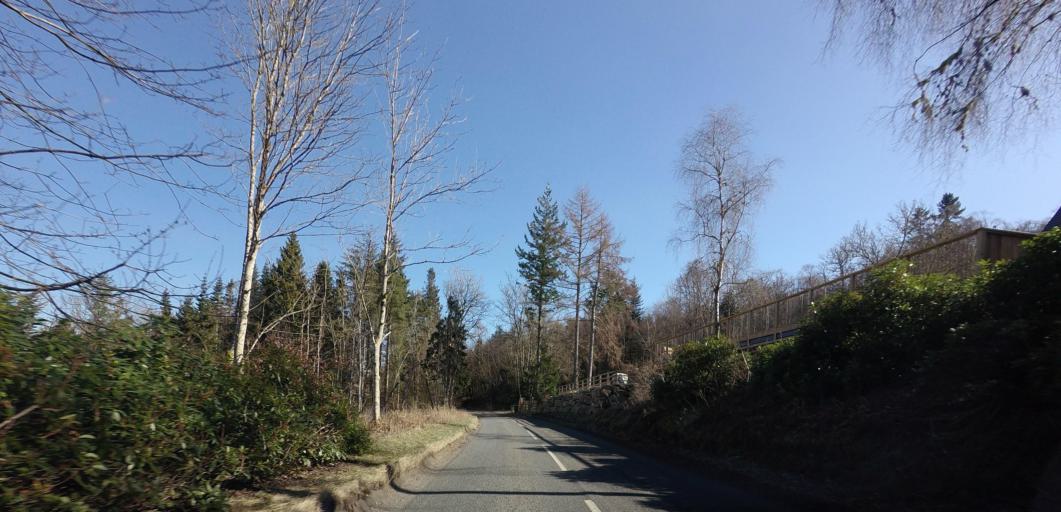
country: GB
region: Scotland
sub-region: Perth and Kinross
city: Bankfoot
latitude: 56.5554
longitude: -3.6131
